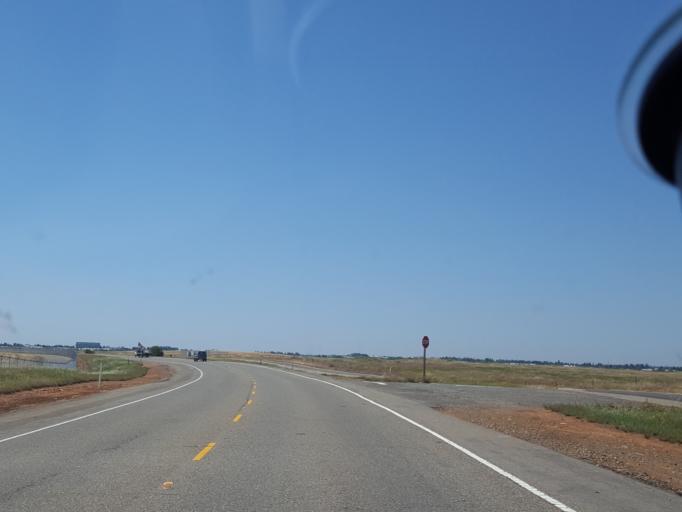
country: US
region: California
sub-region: Sacramento County
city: Rancho Cordova
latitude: 38.5626
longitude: -121.2670
